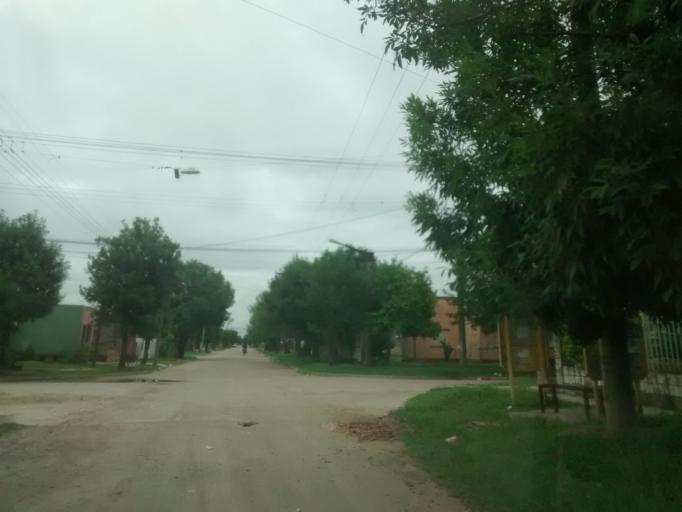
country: AR
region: Chaco
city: Puerto Tirol
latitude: -27.3732
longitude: -59.0995
